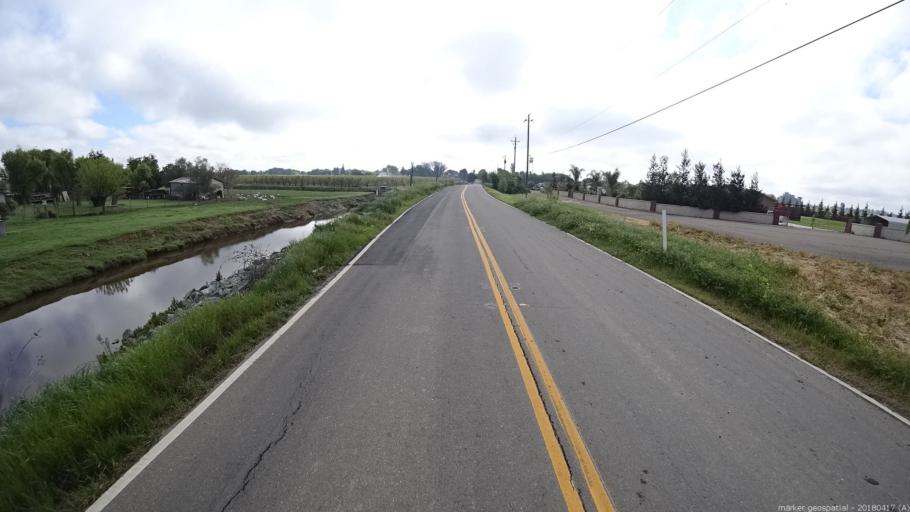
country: US
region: California
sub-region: Sacramento County
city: Walnut Grove
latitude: 38.2396
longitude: -121.5661
